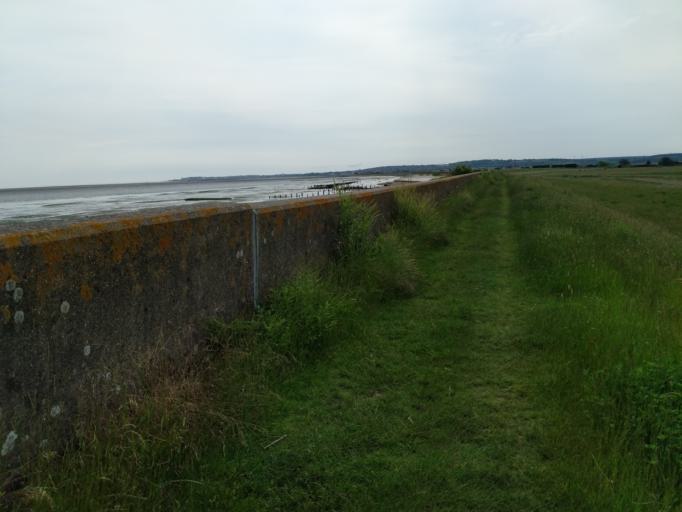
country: GB
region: England
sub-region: Kent
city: Leysdown-on-Sea
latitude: 51.3457
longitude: 0.9470
